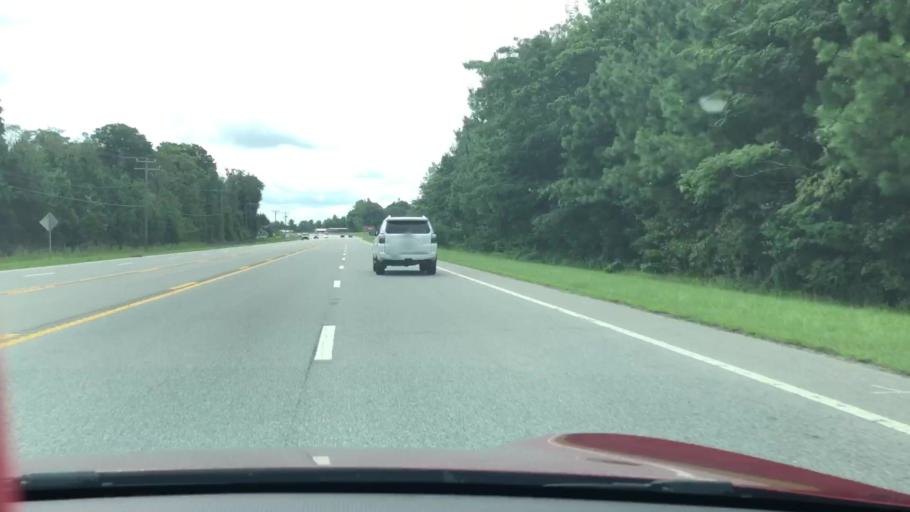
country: US
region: North Carolina
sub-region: Currituck County
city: Moyock
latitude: 36.4842
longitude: -76.1334
